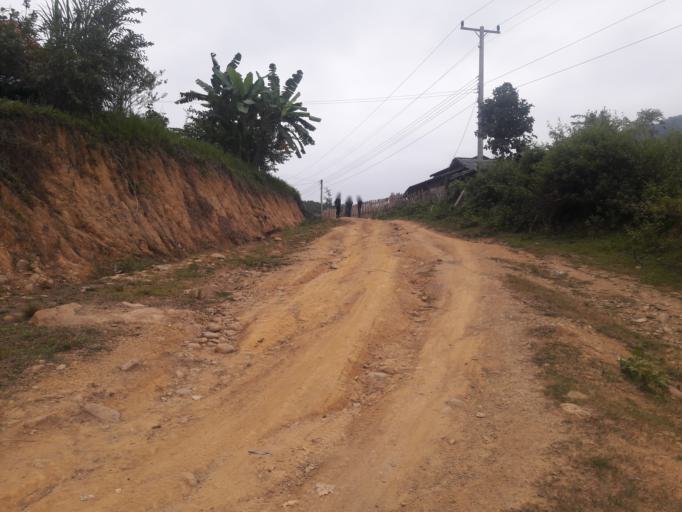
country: LA
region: Xiangkhoang
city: Muang Phonsavan
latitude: 19.3345
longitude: 103.6494
